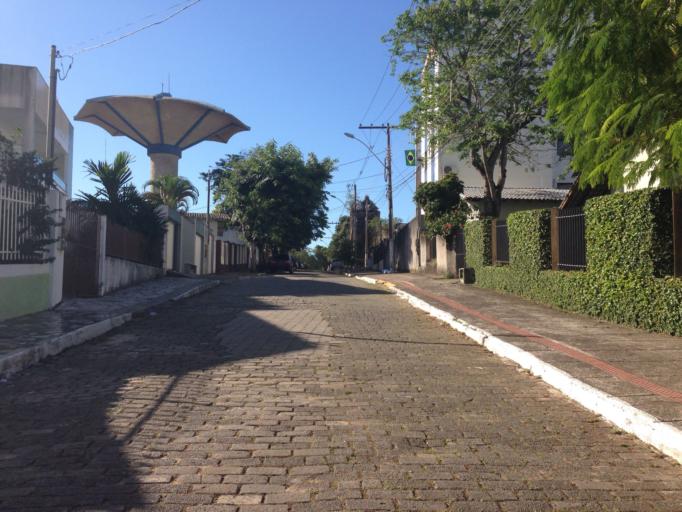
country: BR
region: Espirito Santo
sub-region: Guarapari
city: Guarapari
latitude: -20.6702
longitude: -40.4956
